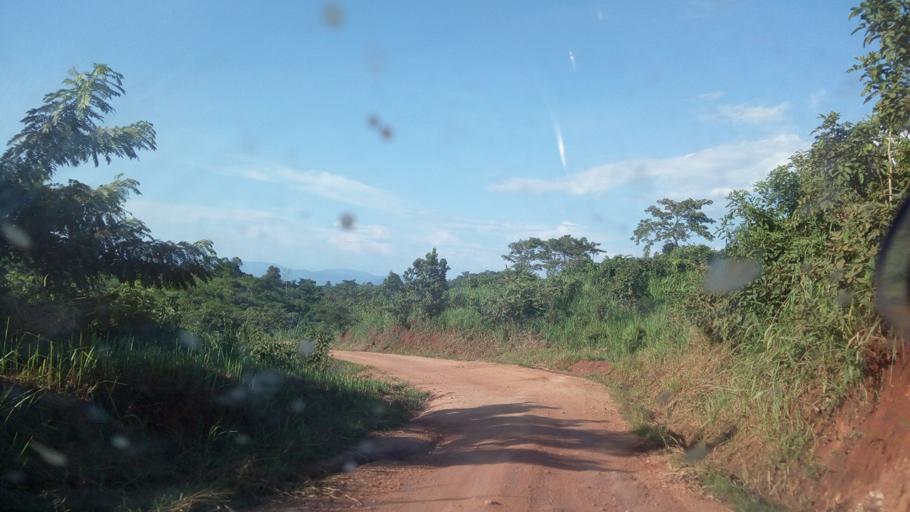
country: BI
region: Bururi
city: Rumonge
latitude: -4.2801
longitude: 28.9688
